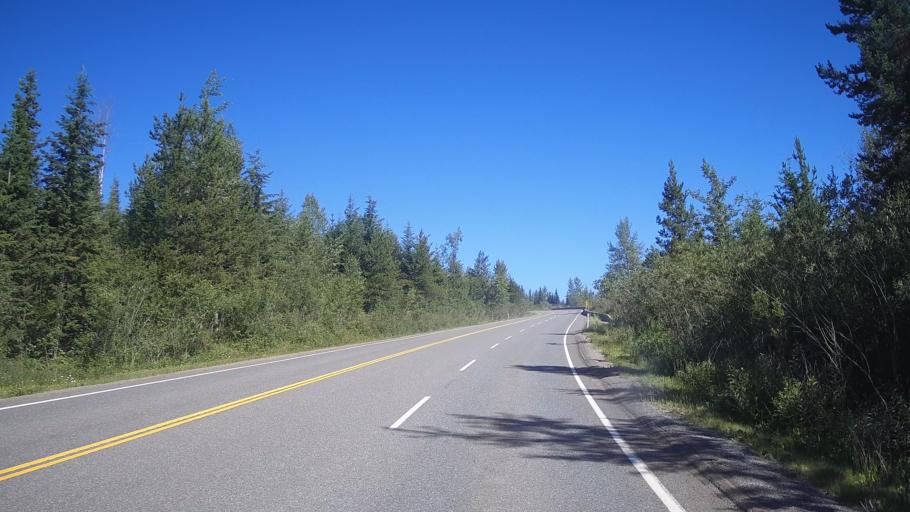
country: CA
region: British Columbia
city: Kamloops
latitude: 51.4892
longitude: -120.3236
